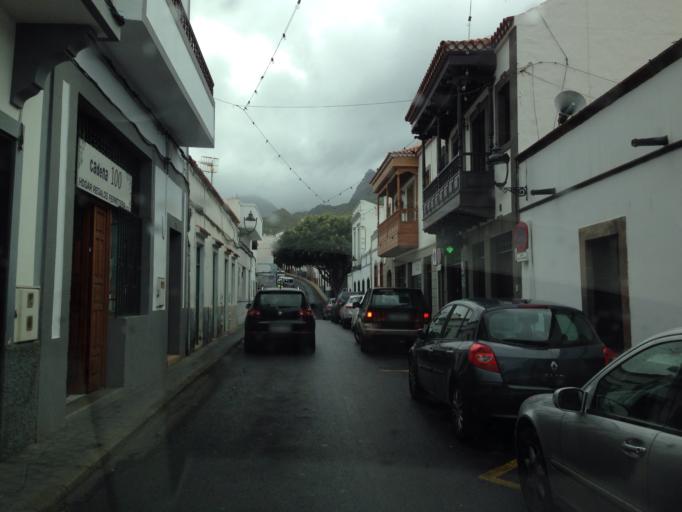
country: ES
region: Canary Islands
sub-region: Provincia de Las Palmas
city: Agaete
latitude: 28.0995
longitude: -15.6998
